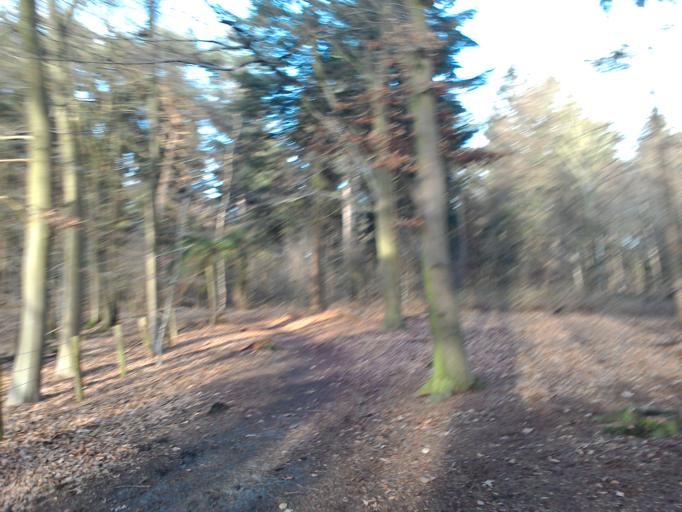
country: NL
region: Utrecht
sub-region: Gemeente De Bilt
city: De Bilt
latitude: 52.1143
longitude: 5.1950
